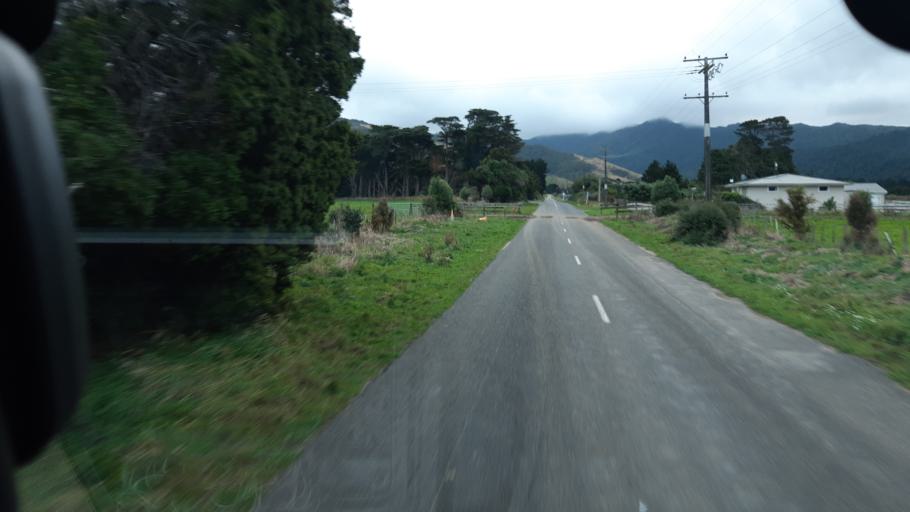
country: NZ
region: Manawatu-Wanganui
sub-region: Palmerston North City
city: Palmerston North
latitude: -40.5738
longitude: 175.6421
